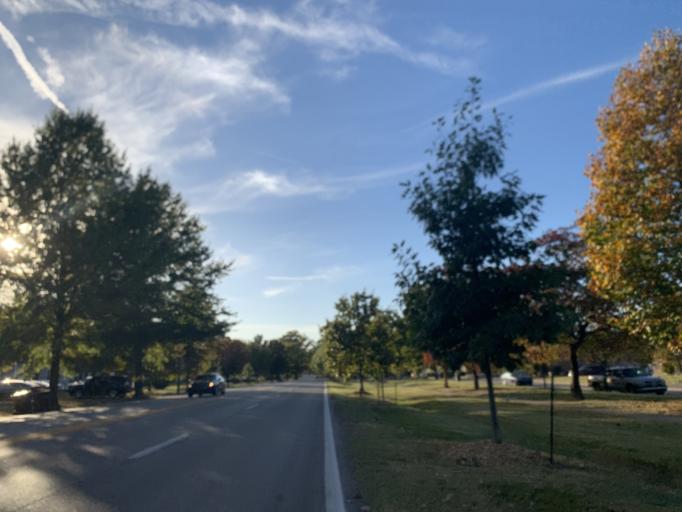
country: US
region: Kentucky
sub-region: Jefferson County
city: Shively
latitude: 38.2251
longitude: -85.8156
